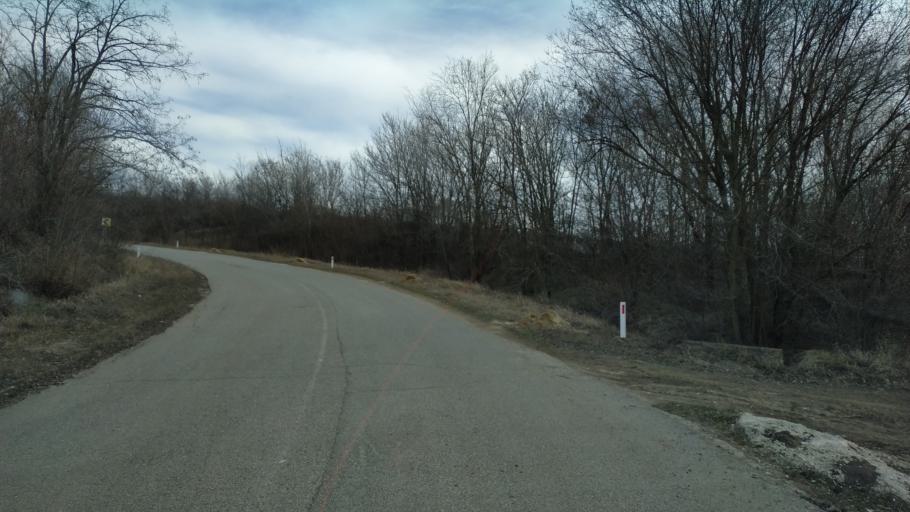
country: MD
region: Nisporeni
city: Nisporeni
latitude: 46.9547
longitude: 28.2314
